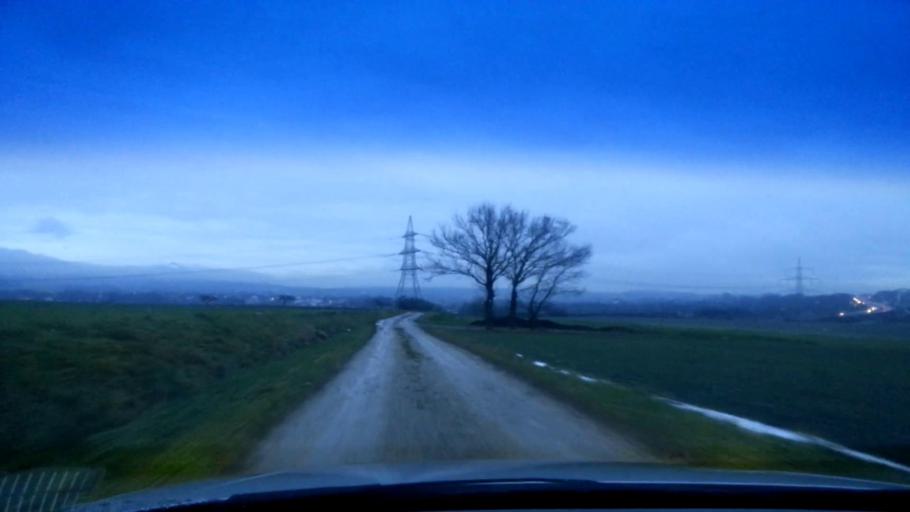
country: DE
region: Bavaria
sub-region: Upper Franconia
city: Schesslitz
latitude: 49.9701
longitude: 10.9946
